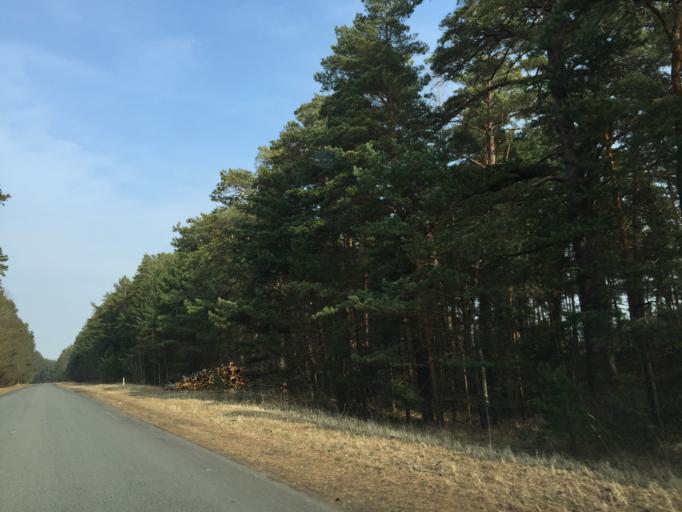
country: LV
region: Salacgrivas
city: Ainazi
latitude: 57.8844
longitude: 24.3666
